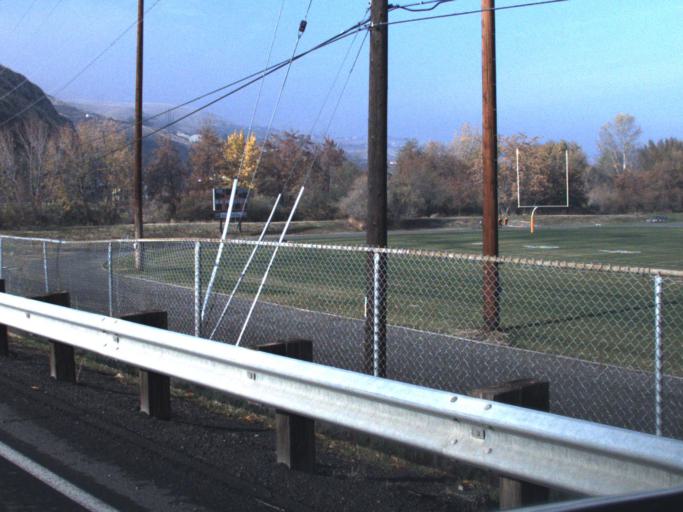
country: US
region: Washington
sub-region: Asotin County
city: Asotin
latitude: 46.3410
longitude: -117.0537
